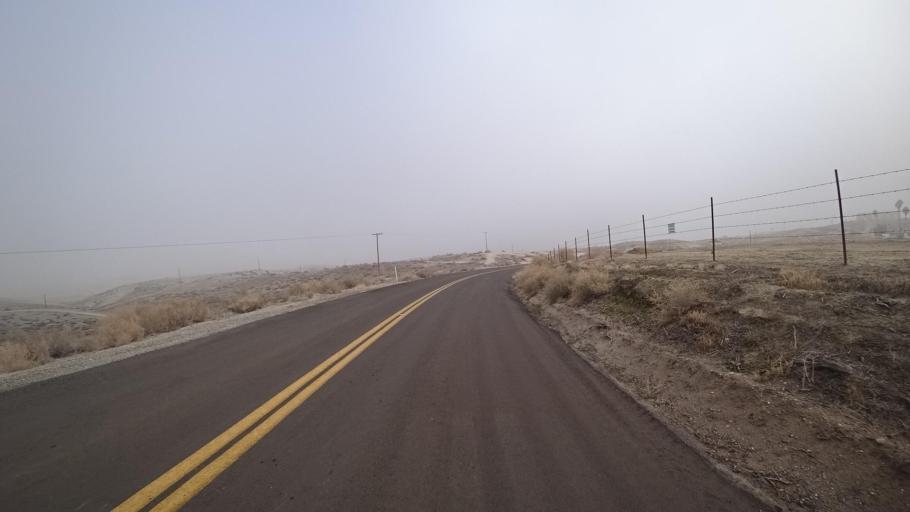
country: US
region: California
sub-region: Kern County
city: Ford City
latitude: 35.1649
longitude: -119.3837
